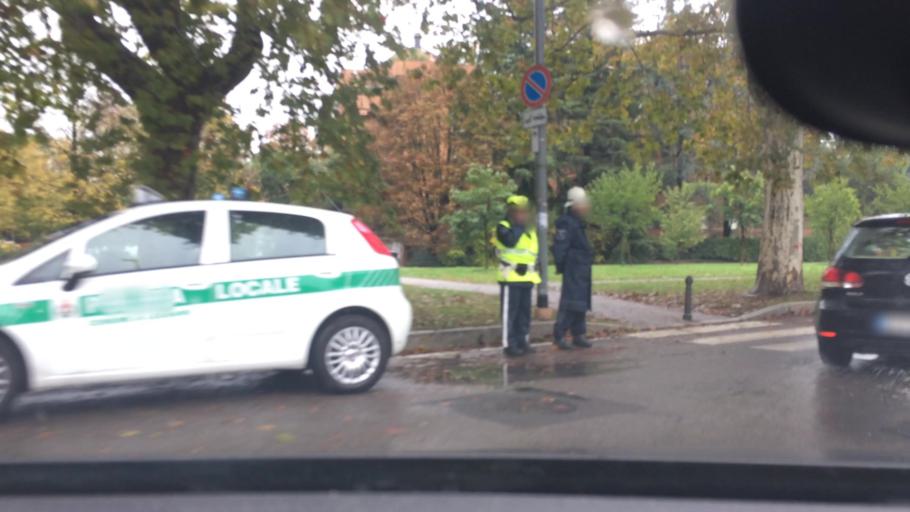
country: IT
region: Lombardy
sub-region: Citta metropolitana di Milano
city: Legnano
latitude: 45.5877
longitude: 8.9199
